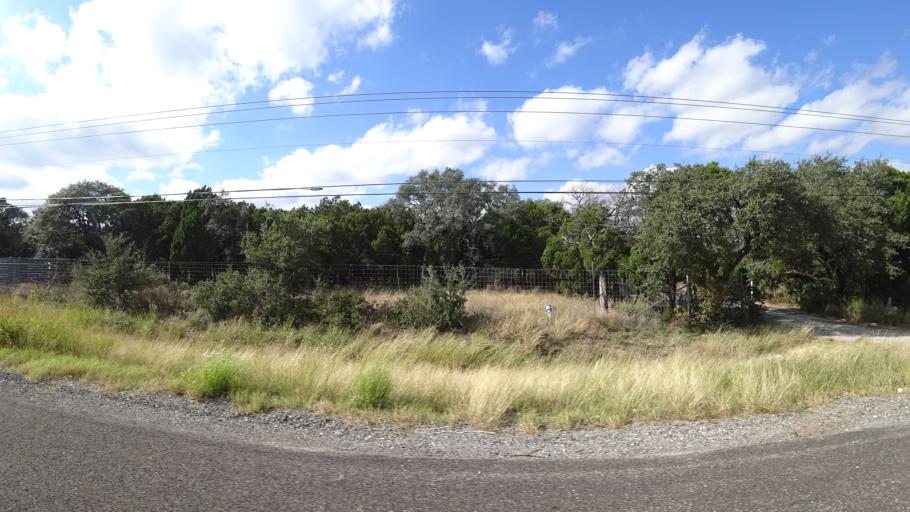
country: US
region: Texas
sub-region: Travis County
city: Bee Cave
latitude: 30.2822
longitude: -97.9170
